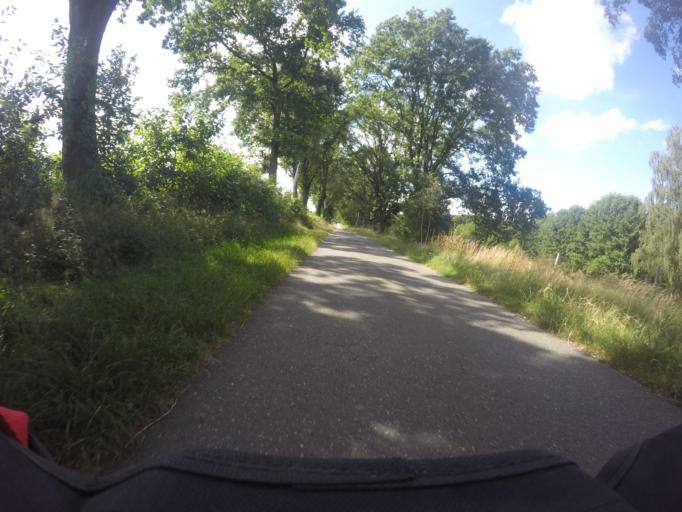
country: DE
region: Lower Saxony
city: Thomasburg
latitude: 53.2264
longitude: 10.6598
